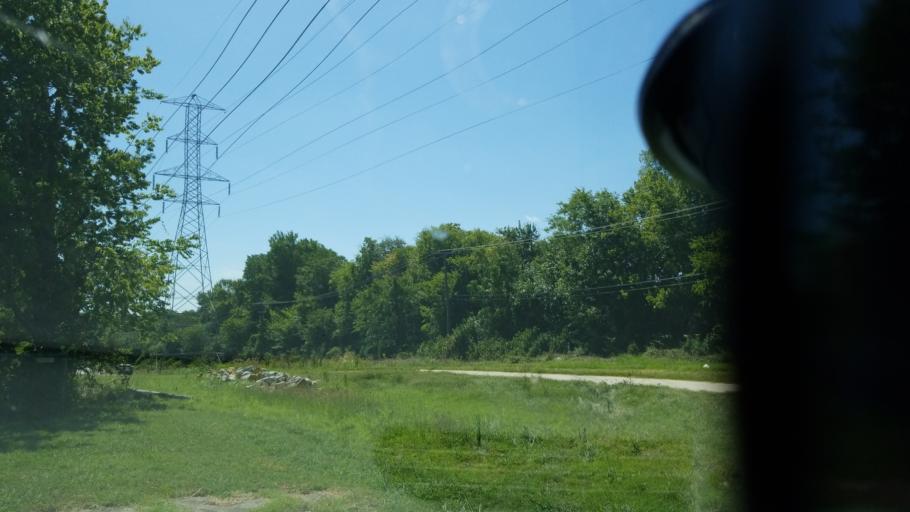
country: US
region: Texas
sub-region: Dallas County
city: Cockrell Hill
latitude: 32.7023
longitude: -96.8206
